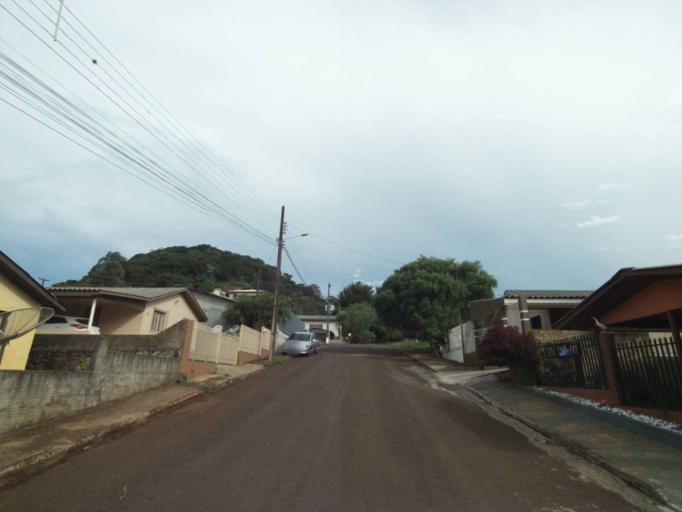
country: BR
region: Parana
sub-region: Guaraniacu
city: Guaraniacu
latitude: -25.1014
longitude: -52.8772
